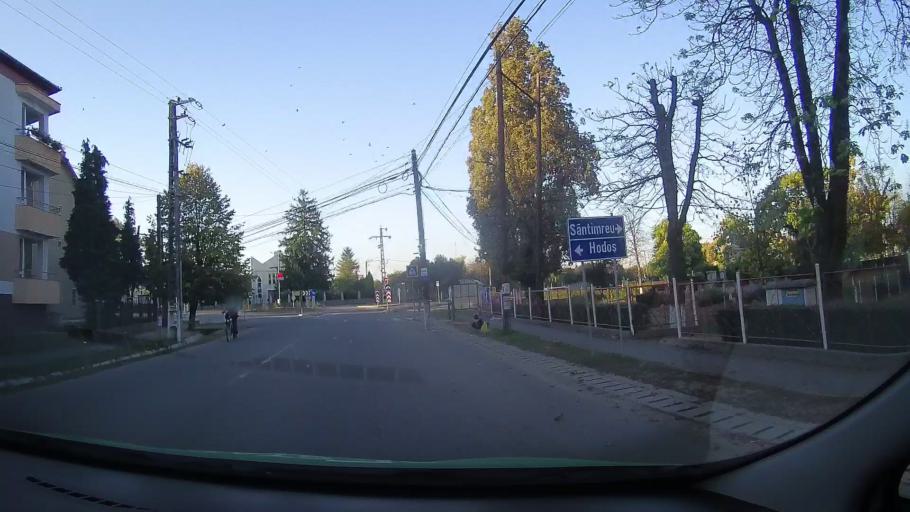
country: RO
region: Bihor
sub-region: Comuna Salard
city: Salard
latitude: 47.2255
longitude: 22.0279
